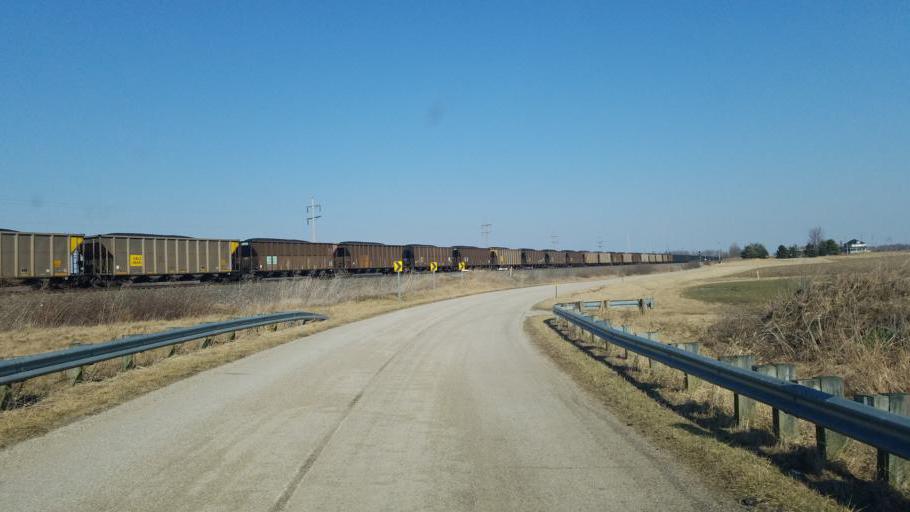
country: US
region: Ohio
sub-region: Crawford County
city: Crestline
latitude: 40.8108
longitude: -82.7163
